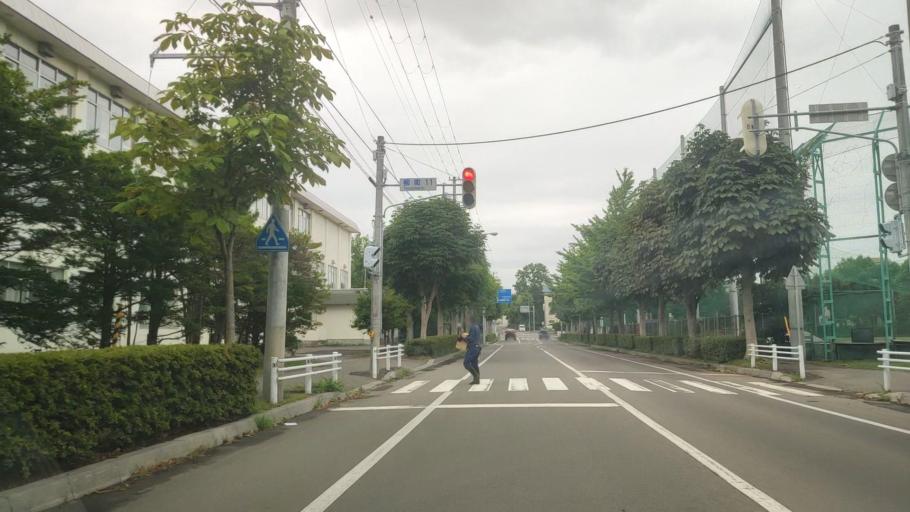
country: JP
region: Hokkaido
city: Hakodate
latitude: 41.7950
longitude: 140.7614
